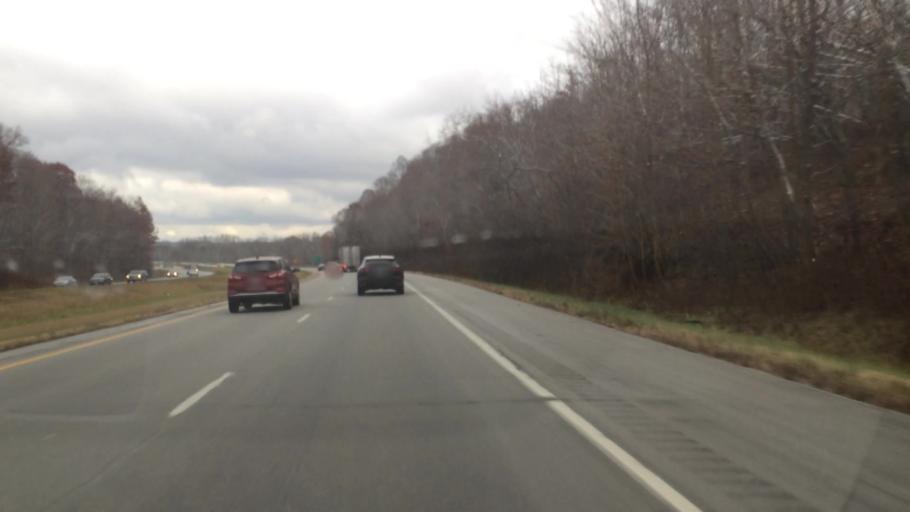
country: US
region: Ohio
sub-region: Summit County
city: Hudson
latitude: 41.2683
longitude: -81.3983
